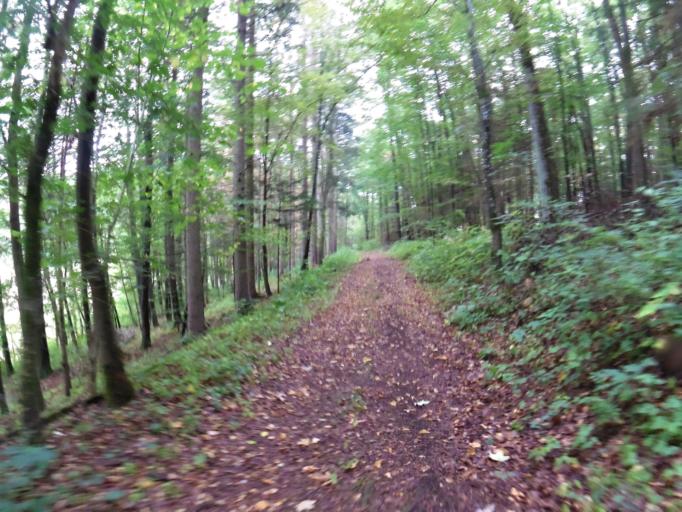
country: DE
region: Bavaria
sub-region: Regierungsbezirk Unterfranken
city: Guntersleben
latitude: 49.8627
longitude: 9.9233
